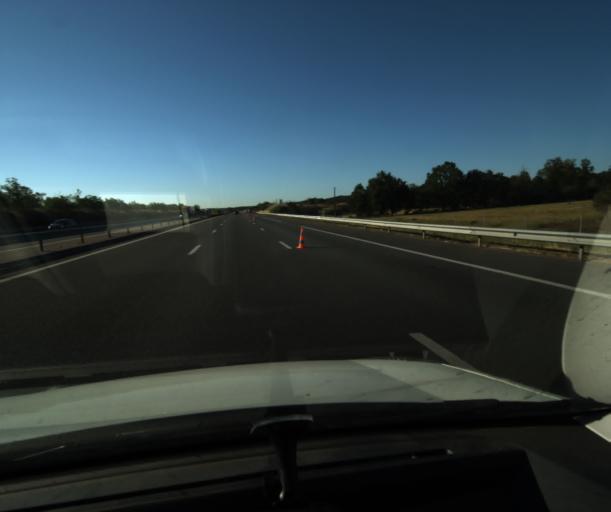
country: FR
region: Midi-Pyrenees
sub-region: Departement du Tarn-et-Garonne
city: Pompignan
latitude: 43.8280
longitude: 1.3432
